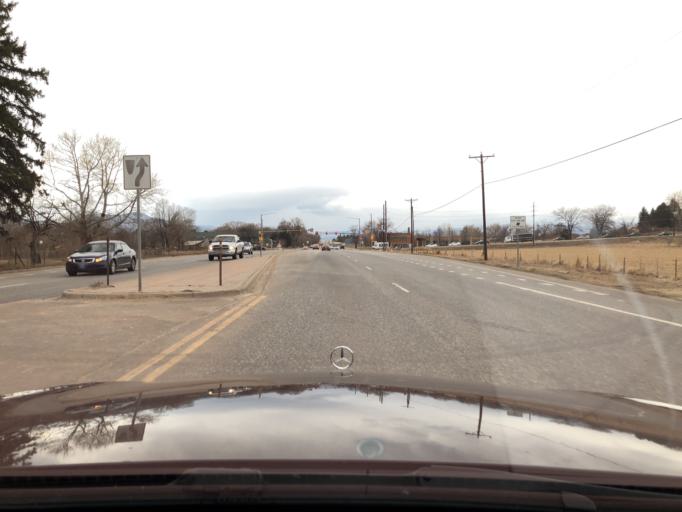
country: US
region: Colorado
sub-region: Boulder County
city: Gunbarrel
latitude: 40.0147
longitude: -105.1756
